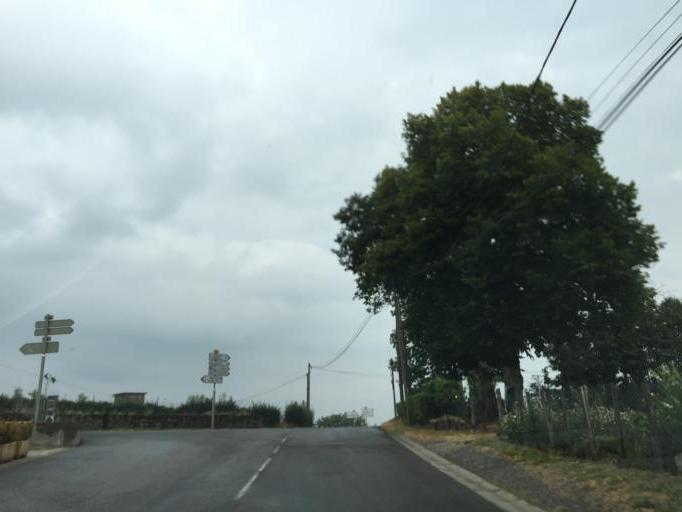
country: FR
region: Rhone-Alpes
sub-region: Departement de la Loire
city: Saint-Christo-en-Jarez
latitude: 45.5357
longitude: 4.4869
